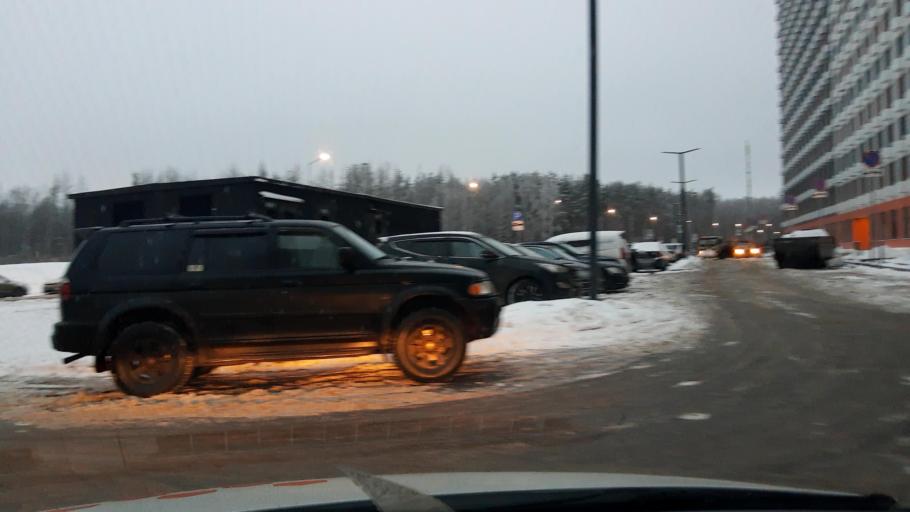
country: RU
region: Moscow
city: Solntsevo
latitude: 55.6163
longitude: 37.4071
